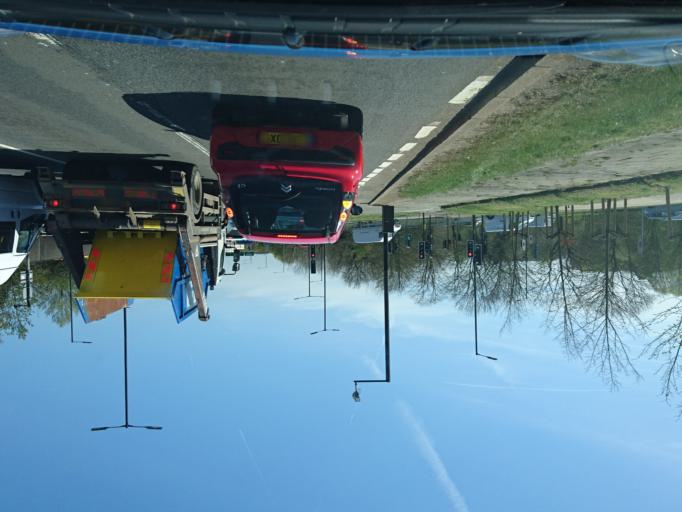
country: GB
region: England
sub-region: Greater London
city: Hendon
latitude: 51.5896
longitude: -0.1952
